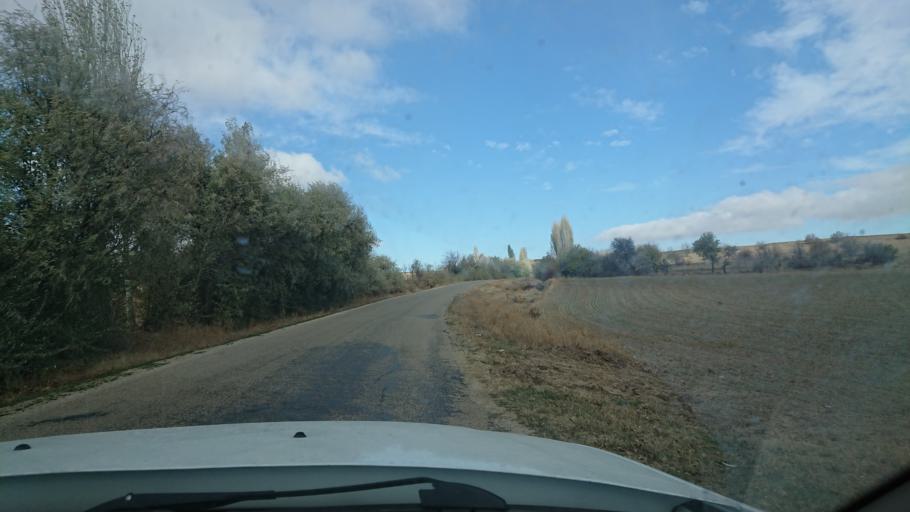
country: TR
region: Aksaray
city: Agacoren
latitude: 38.8303
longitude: 33.9562
